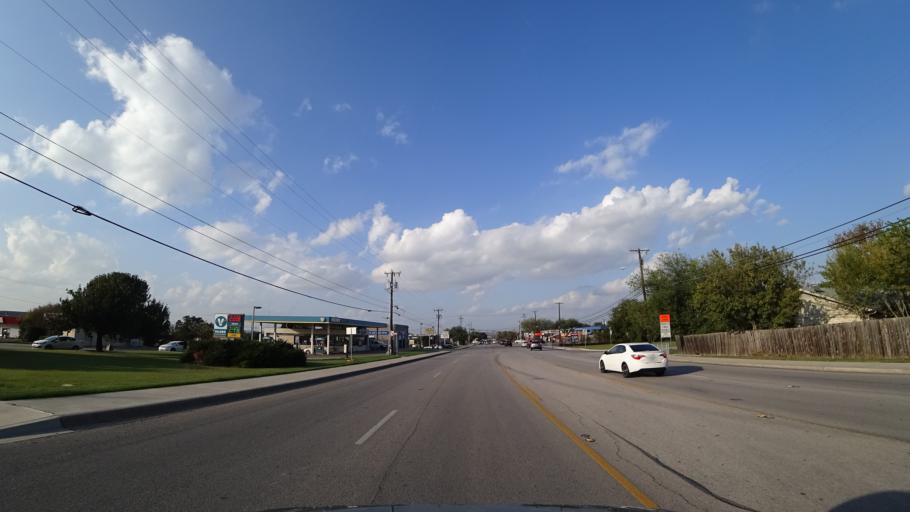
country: US
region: Texas
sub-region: Williamson County
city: Round Rock
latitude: 30.4919
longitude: -97.6757
